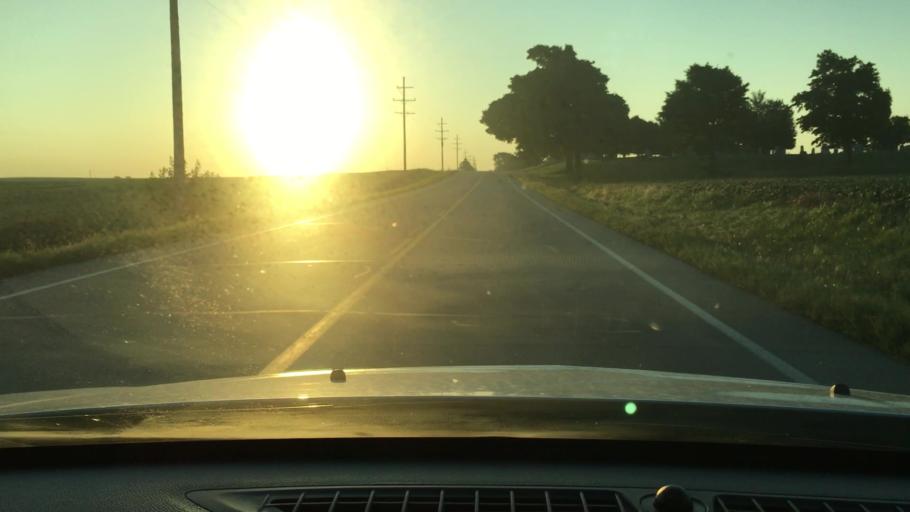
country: US
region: Illinois
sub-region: DeKalb County
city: Waterman
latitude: 41.8491
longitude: -88.7811
